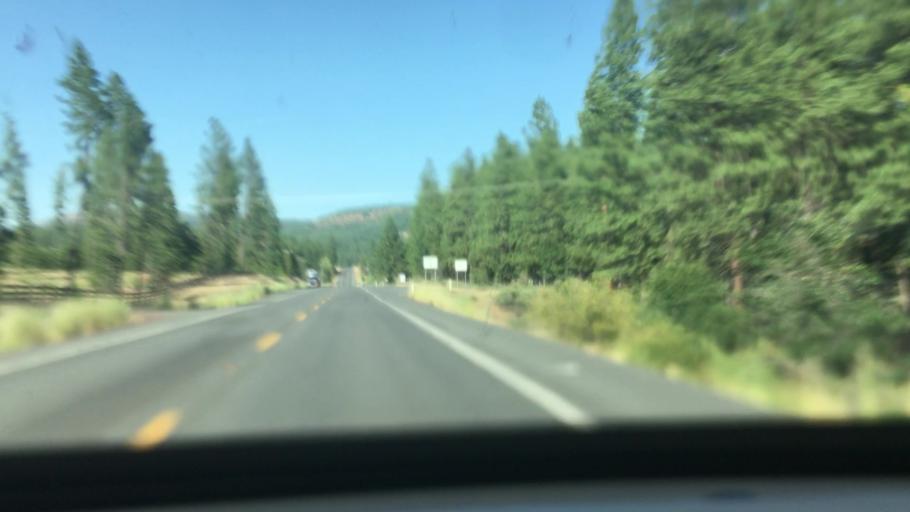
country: US
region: Washington
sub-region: Klickitat County
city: Goldendale
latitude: 45.9404
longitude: -120.6824
